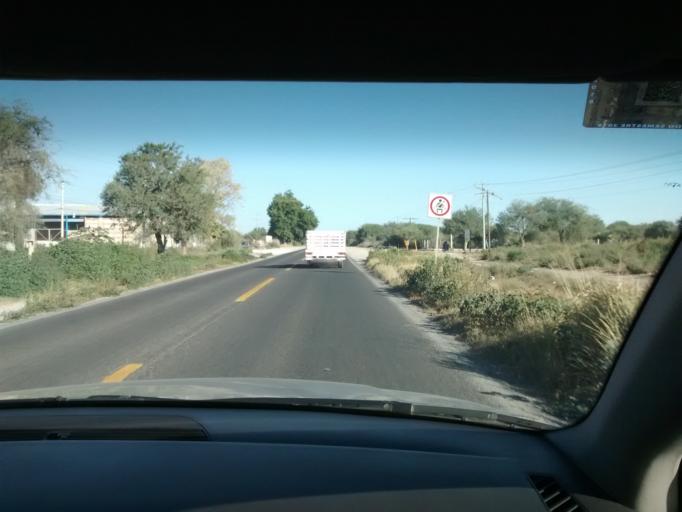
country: MX
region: Puebla
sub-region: Santiago Miahuatlan
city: San Jose Monte Chiquito
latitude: 18.4969
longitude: -97.4712
